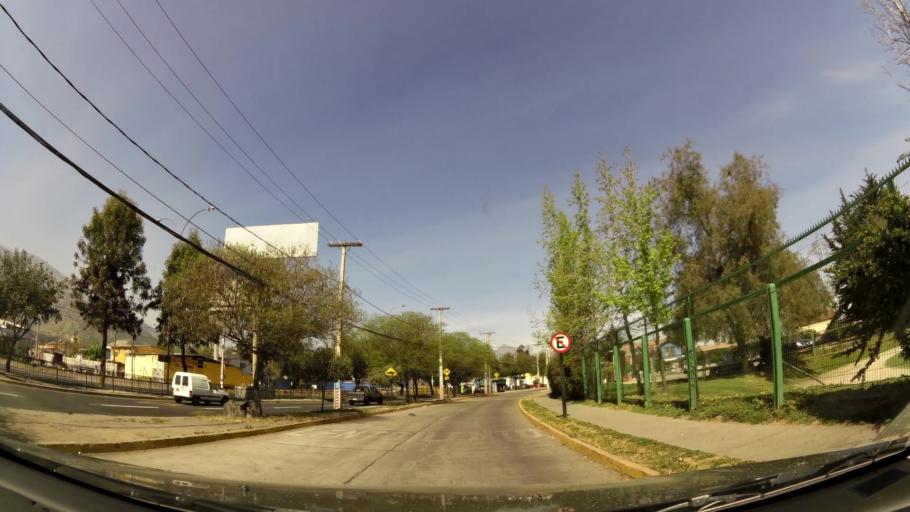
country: CL
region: Santiago Metropolitan
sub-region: Provincia de Cordillera
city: Puente Alto
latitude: -33.5625
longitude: -70.5558
